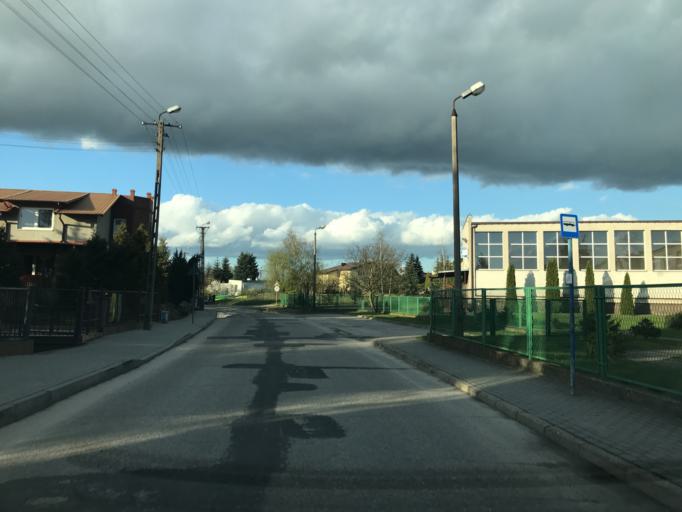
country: PL
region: Kujawsko-Pomorskie
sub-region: Powiat brodnicki
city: Brodnica
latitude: 53.2501
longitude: 19.4166
